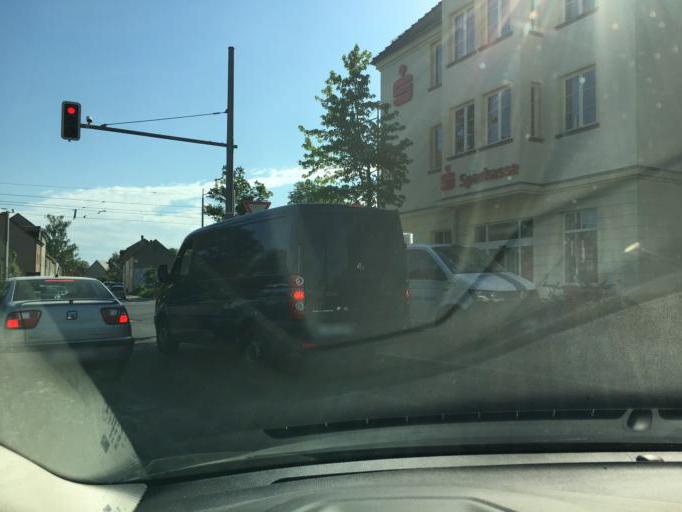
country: DE
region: Saxony
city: Markkleeberg
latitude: 51.3045
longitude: 12.4243
